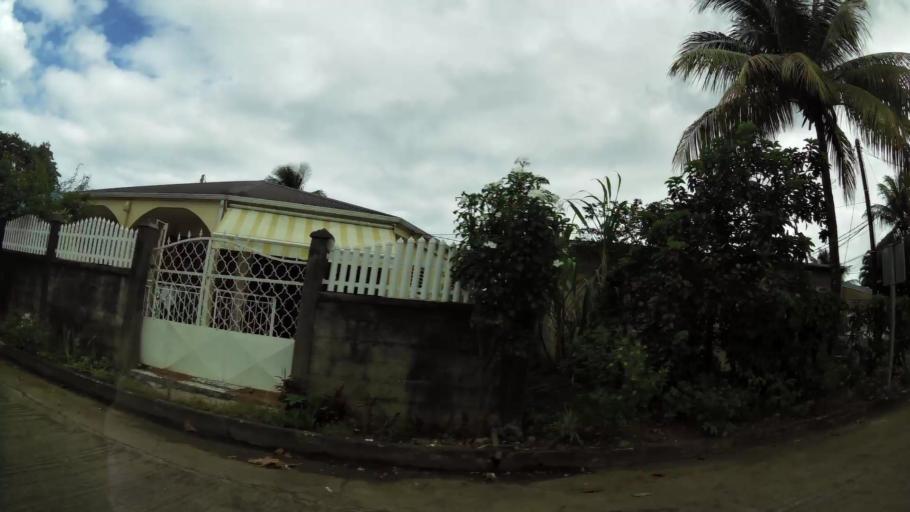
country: GP
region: Guadeloupe
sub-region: Guadeloupe
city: Sainte-Rose
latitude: 16.3035
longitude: -61.6718
